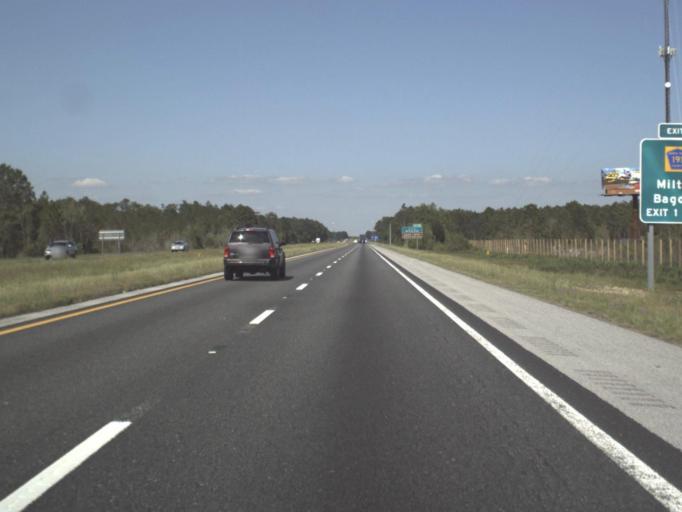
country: US
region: Florida
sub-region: Santa Rosa County
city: Bagdad
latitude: 30.5576
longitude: -87.0472
